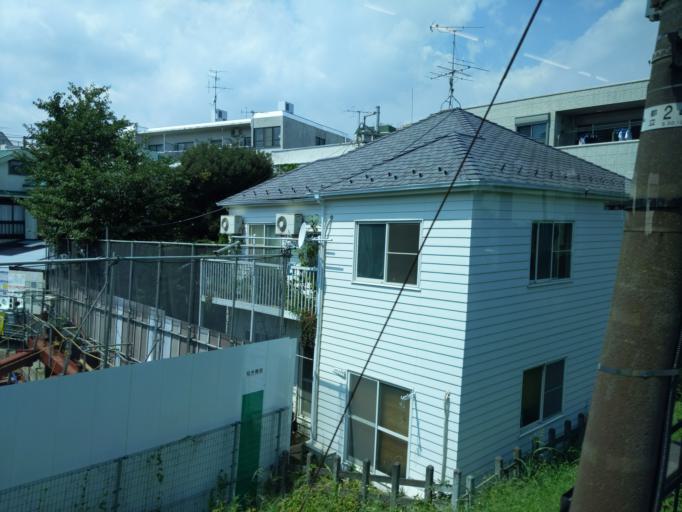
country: JP
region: Tokyo
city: Tokyo
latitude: 35.6104
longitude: 139.6704
